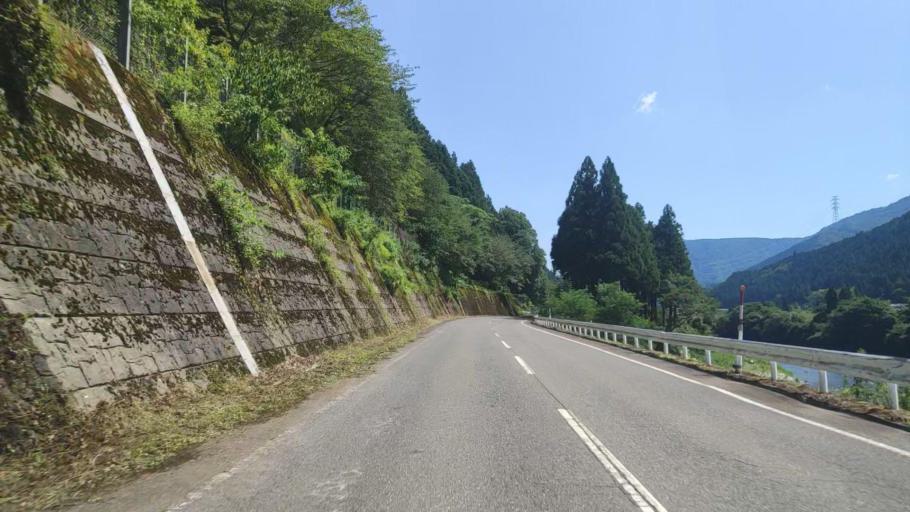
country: JP
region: Gifu
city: Godo
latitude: 35.6066
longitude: 136.6279
